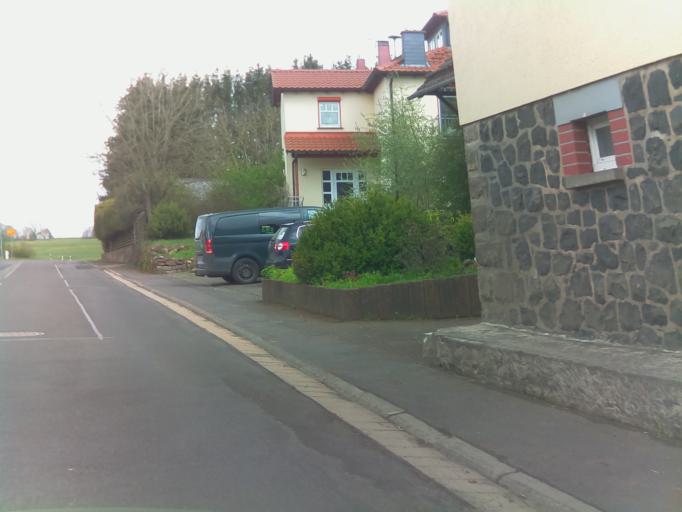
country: DE
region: Hesse
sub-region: Regierungsbezirk Giessen
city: Grebenhain
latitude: 50.4568
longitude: 9.3682
